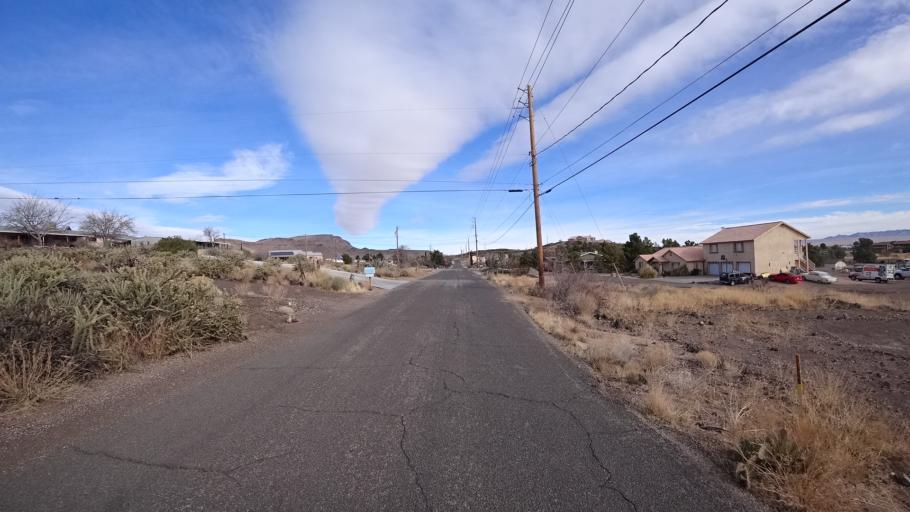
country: US
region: Arizona
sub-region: Mohave County
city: Kingman
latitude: 35.2249
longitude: -114.0470
